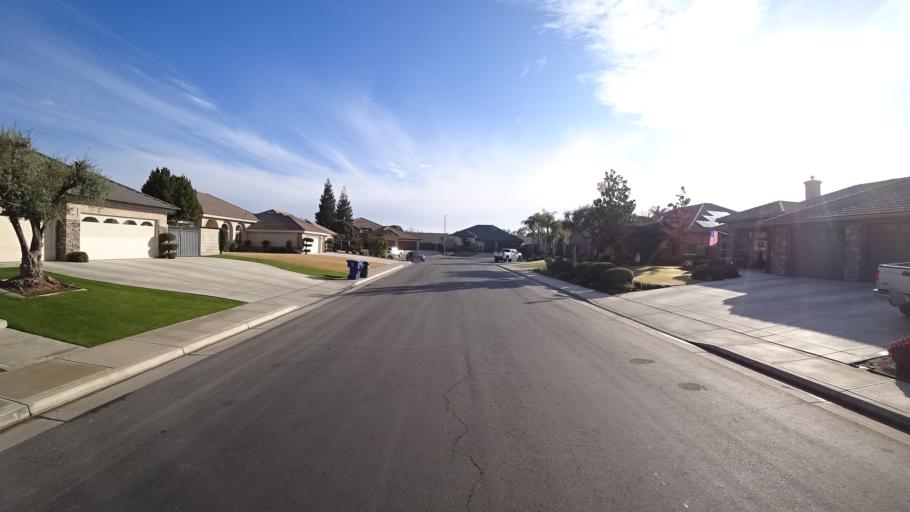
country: US
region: California
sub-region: Kern County
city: Rosedale
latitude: 35.4102
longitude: -119.1331
